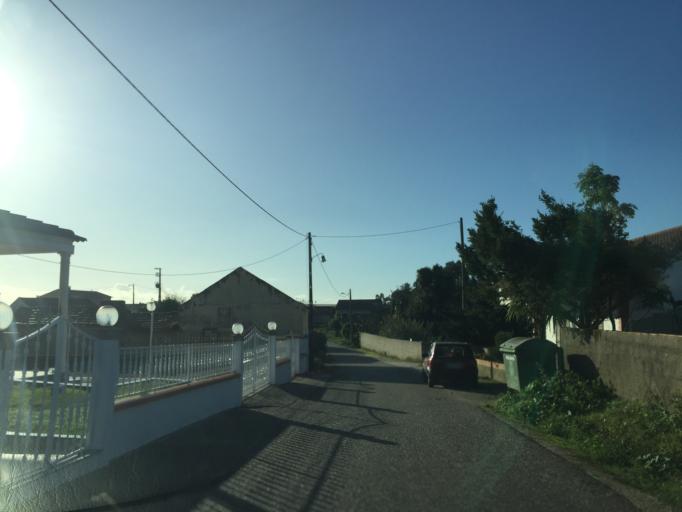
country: PT
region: Coimbra
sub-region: Figueira da Foz
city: Lavos
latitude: 40.0524
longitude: -8.7917
